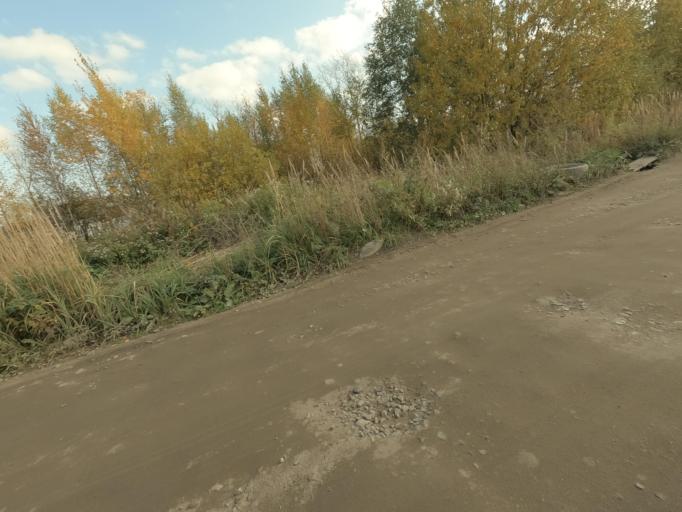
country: RU
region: Leningrad
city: Mga
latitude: 59.7515
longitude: 31.0756
